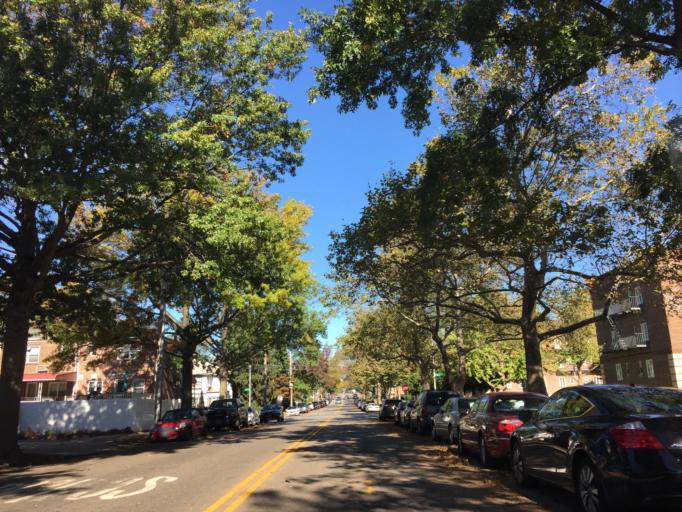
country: US
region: New York
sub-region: Nassau County
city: East Atlantic Beach
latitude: 40.7597
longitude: -73.7740
